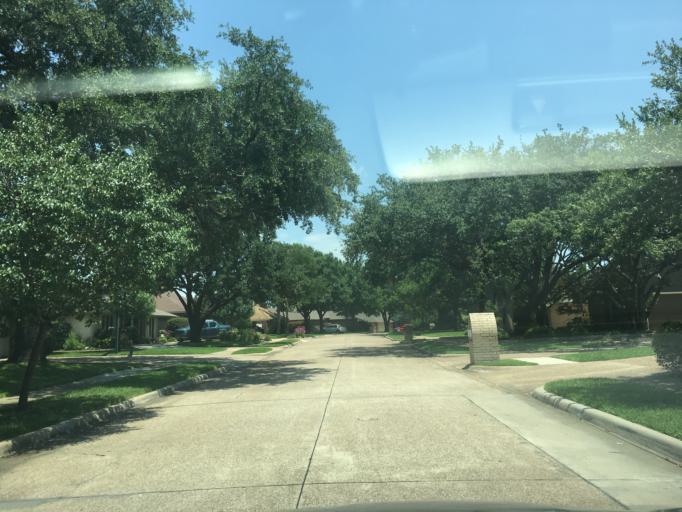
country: US
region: Texas
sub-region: Dallas County
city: Carrollton
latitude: 32.9480
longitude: -96.8689
